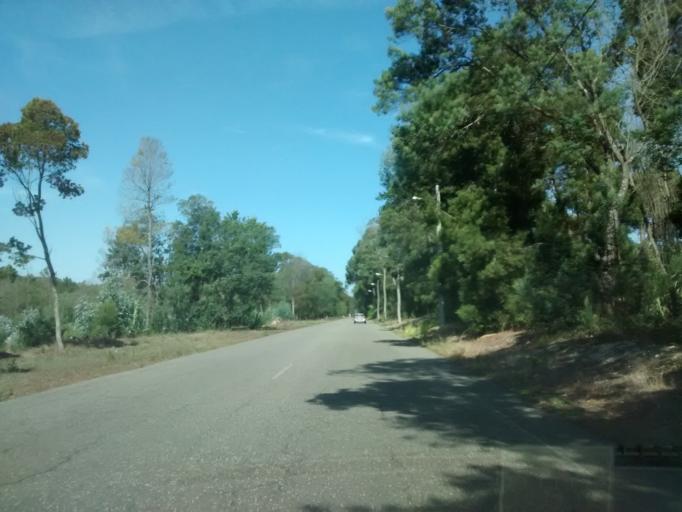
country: PT
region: Coimbra
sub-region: Mira
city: Mira
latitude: 40.4488
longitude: -8.7658
